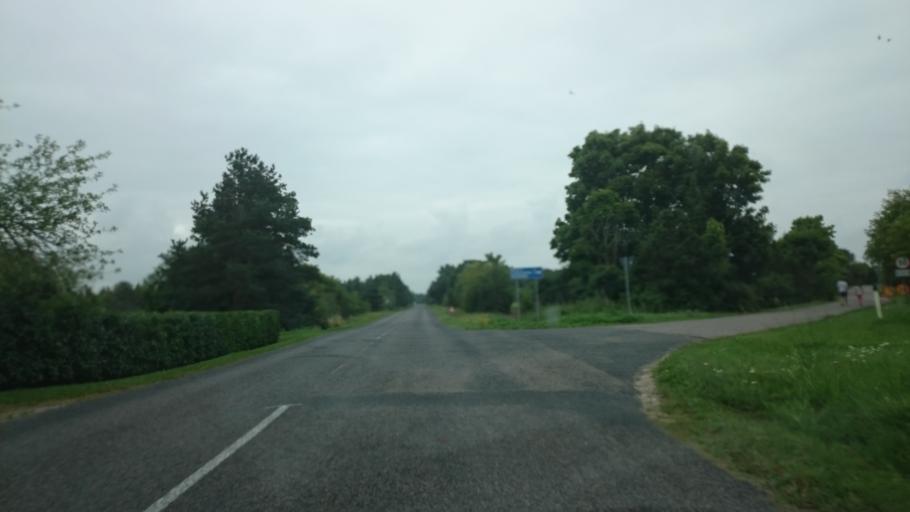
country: EE
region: Saare
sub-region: Orissaare vald
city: Orissaare
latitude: 58.5814
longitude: 23.0271
